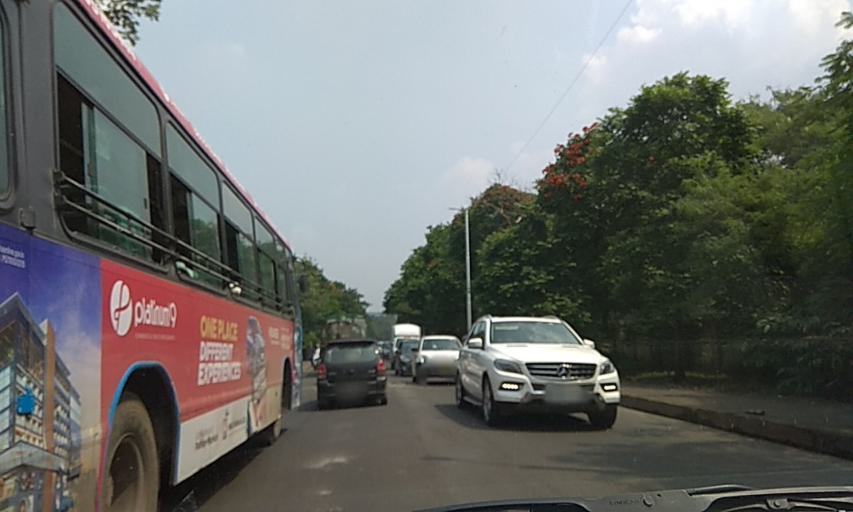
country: IN
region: Maharashtra
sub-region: Pune Division
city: Shivaji Nagar
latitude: 18.5381
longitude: 73.7992
